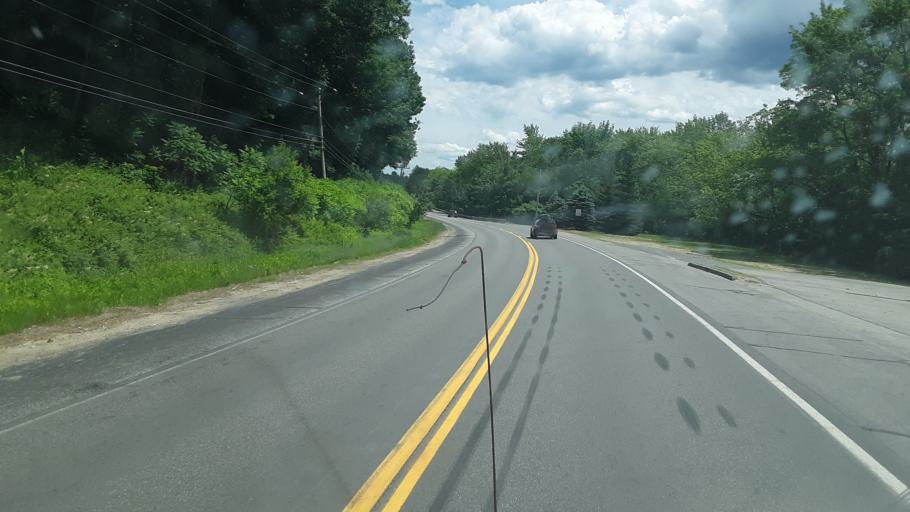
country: US
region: Maine
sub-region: Oxford County
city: Mexico
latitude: 44.5430
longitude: -70.5260
